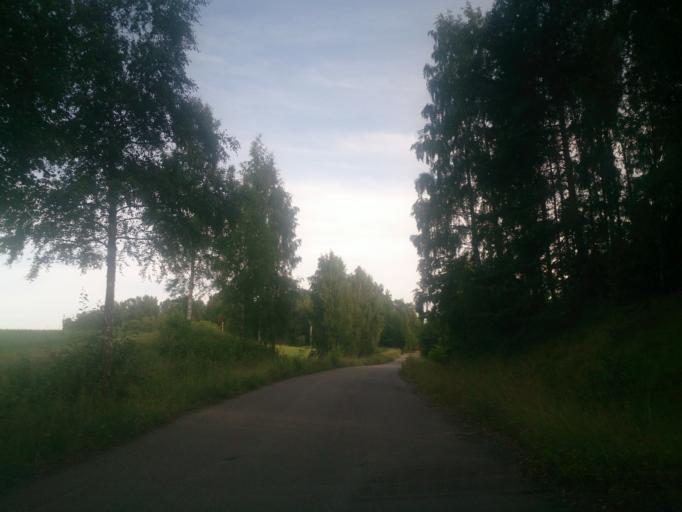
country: SE
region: OEstergoetland
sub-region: Atvidabergs Kommun
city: Atvidaberg
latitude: 58.2373
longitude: 15.9650
